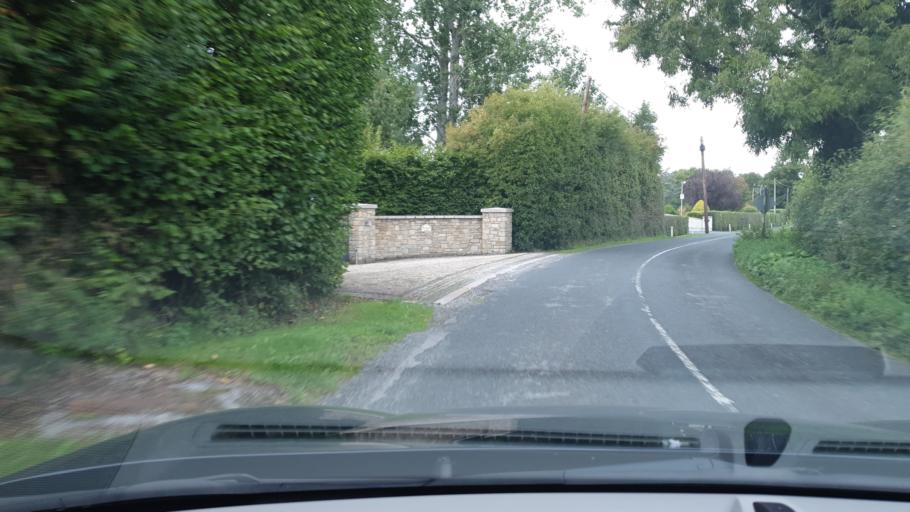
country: IE
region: Leinster
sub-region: Kildare
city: Clane
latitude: 53.3182
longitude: -6.6386
